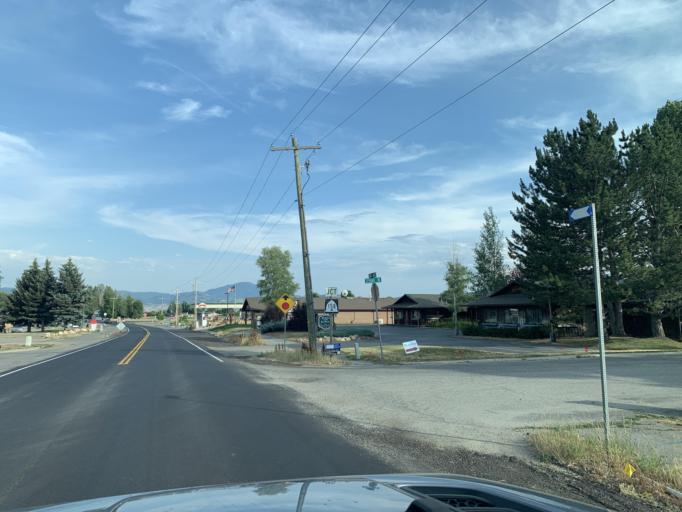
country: US
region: Utah
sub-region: Weber County
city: Wolf Creek
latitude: 41.3063
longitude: -111.8287
